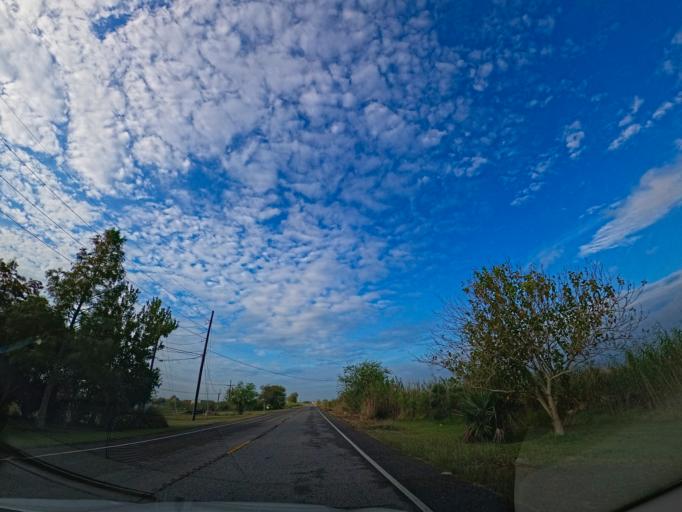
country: US
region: Louisiana
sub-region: Terrebonne Parish
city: Dulac
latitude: 29.3442
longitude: -90.6320
